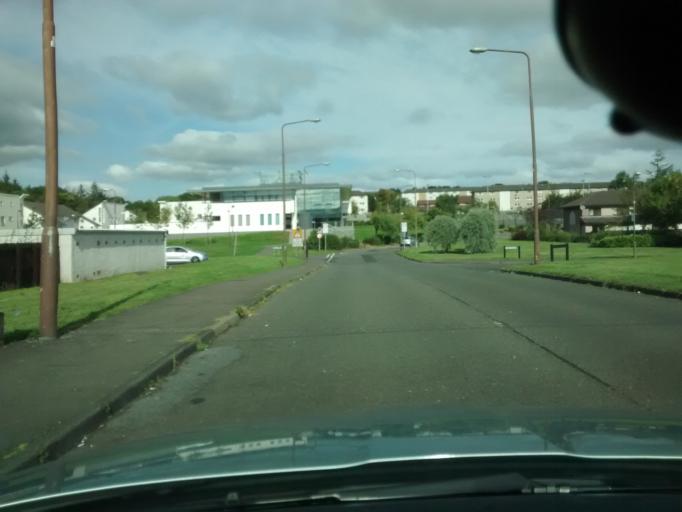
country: GB
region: Scotland
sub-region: West Lothian
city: Mid Calder
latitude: 55.8931
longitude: -3.5016
